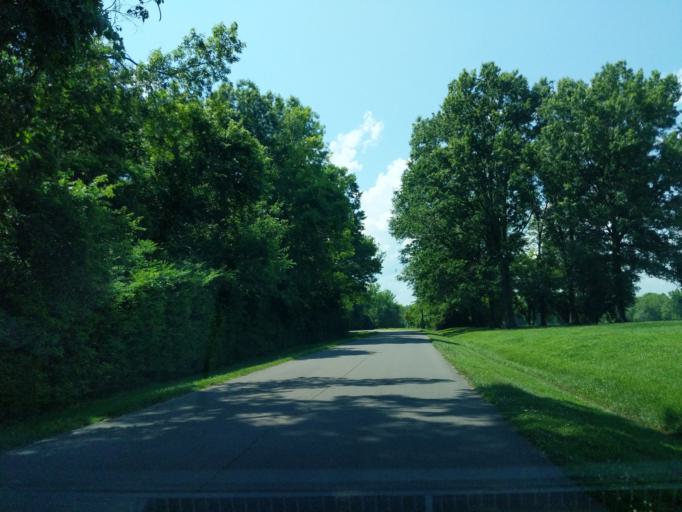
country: US
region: Tennessee
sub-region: Sumner County
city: Hendersonville
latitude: 36.2972
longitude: -86.6614
